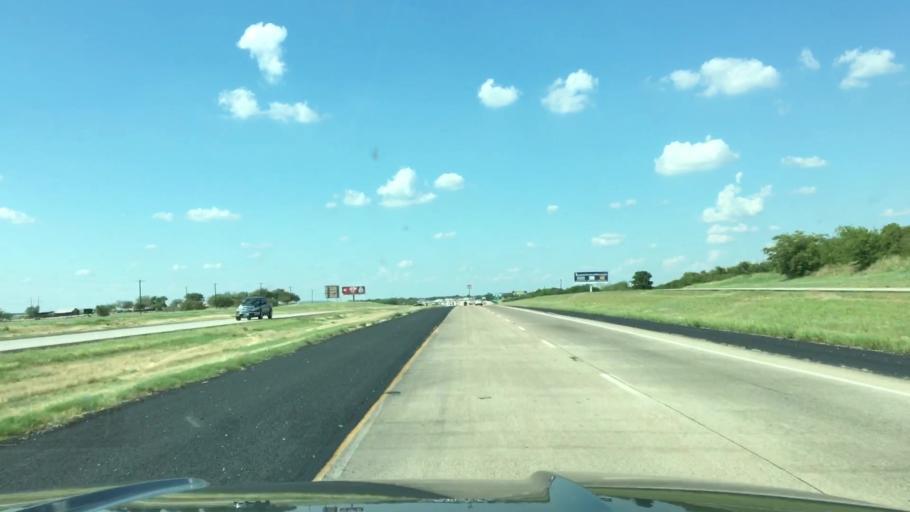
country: US
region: Texas
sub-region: Wise County
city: New Fairview
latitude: 33.0854
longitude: -97.4721
